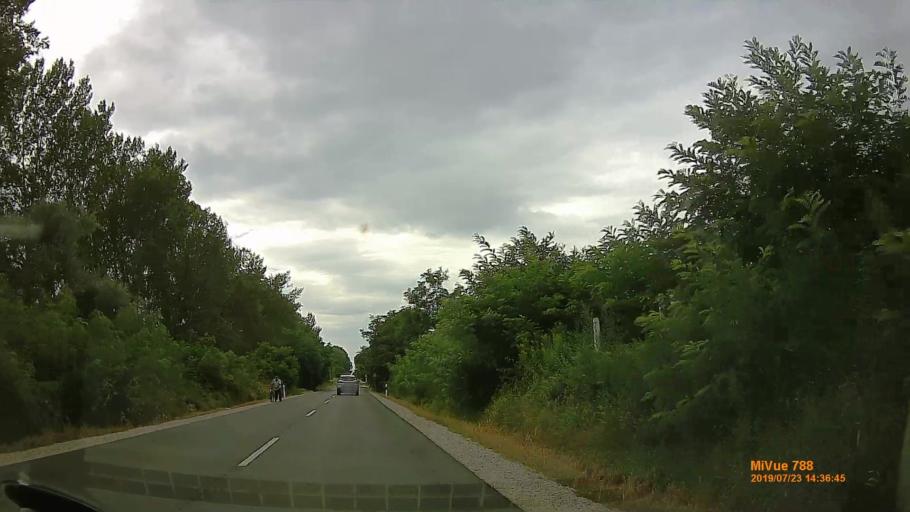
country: HU
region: Szabolcs-Szatmar-Bereg
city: Nyiregyhaza
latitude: 47.9317
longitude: 21.6939
